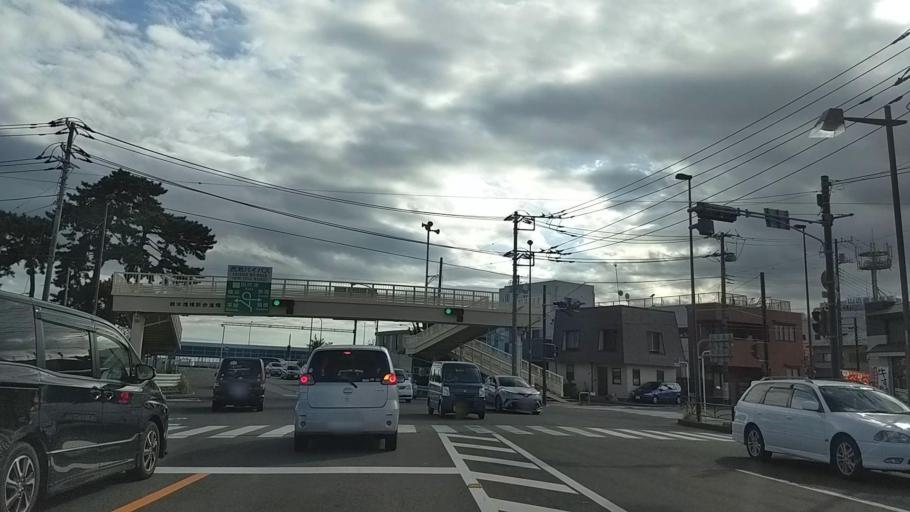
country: JP
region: Kanagawa
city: Odawara
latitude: 35.2785
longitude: 139.2048
